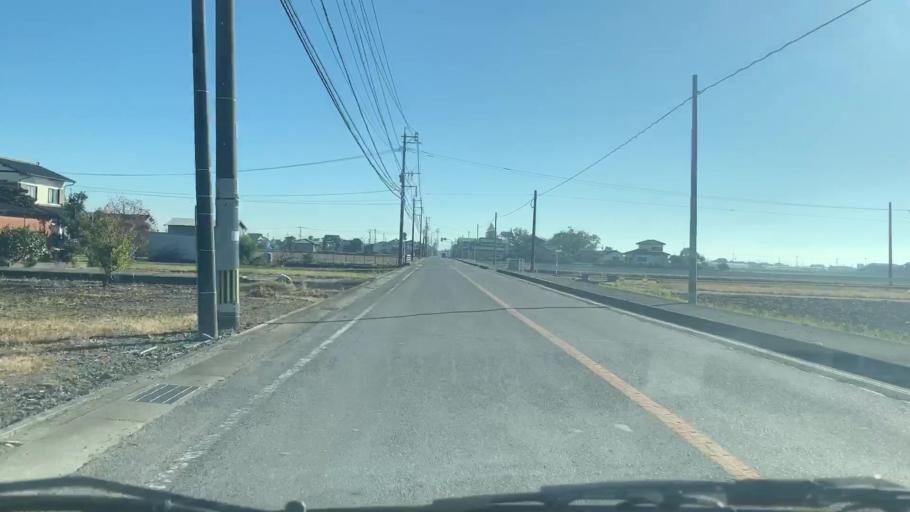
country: JP
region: Saga Prefecture
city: Kashima
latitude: 33.1839
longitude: 130.1680
